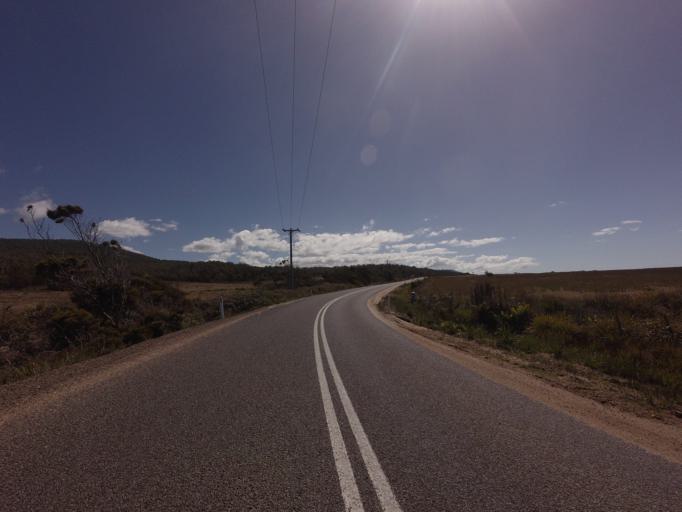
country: AU
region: Tasmania
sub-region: Break O'Day
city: St Helens
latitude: -41.8023
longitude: 148.2617
